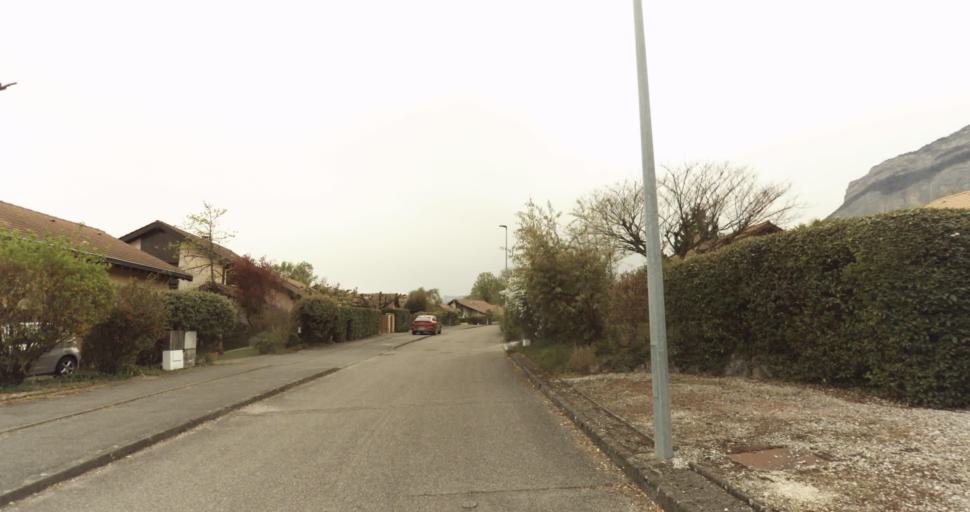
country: FR
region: Rhone-Alpes
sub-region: Departement de l'Isere
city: Saint-Ismier
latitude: 45.2352
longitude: 5.8170
